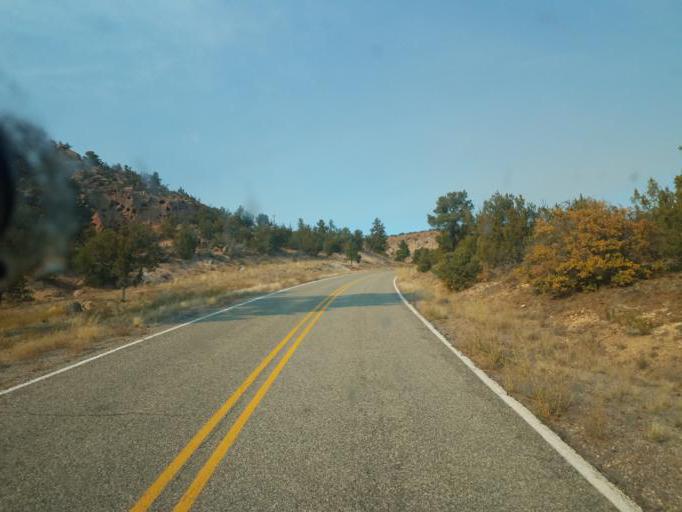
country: US
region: New Mexico
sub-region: Los Alamos County
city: White Rock
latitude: 35.8069
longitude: -106.2487
